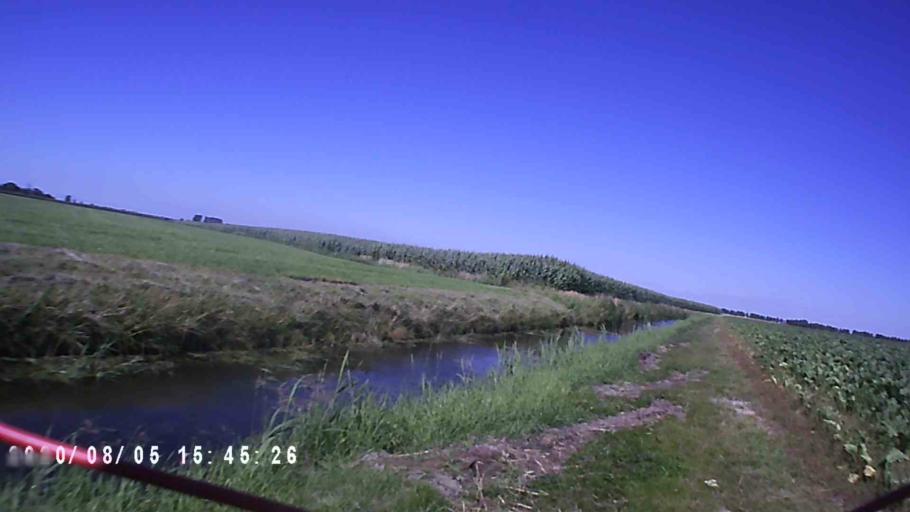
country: NL
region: Groningen
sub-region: Gemeente Winsum
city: Winsum
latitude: 53.3728
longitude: 6.4908
